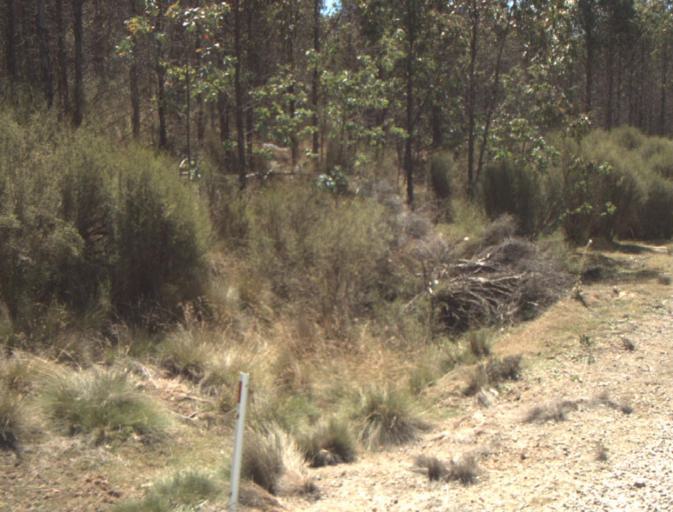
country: AU
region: Tasmania
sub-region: Dorset
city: Scottsdale
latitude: -41.3073
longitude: 147.4662
